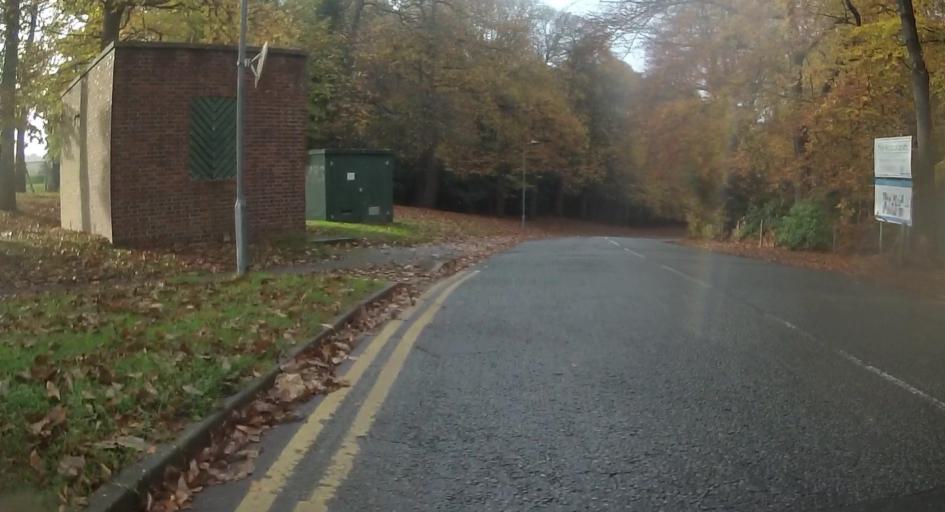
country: GB
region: England
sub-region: Bracknell Forest
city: Crowthorne
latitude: 51.3692
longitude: -0.7826
